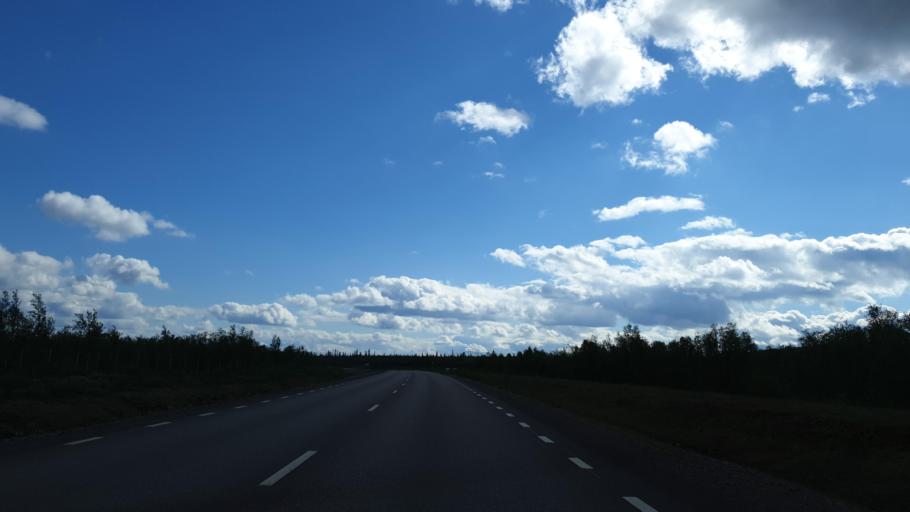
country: SE
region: Norrbotten
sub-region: Kiruna Kommun
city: Kiruna
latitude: 67.8130
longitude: 20.2379
